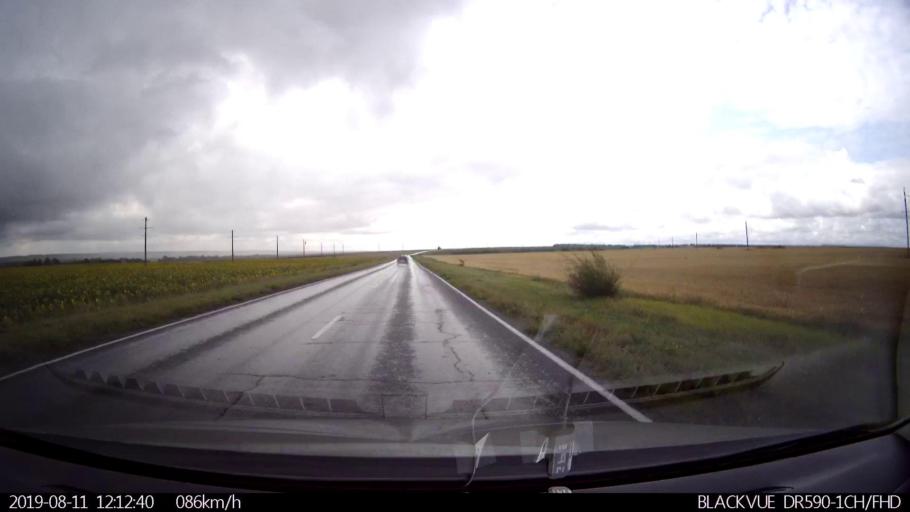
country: RU
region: Ulyanovsk
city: Silikatnyy
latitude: 53.9702
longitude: 47.9956
